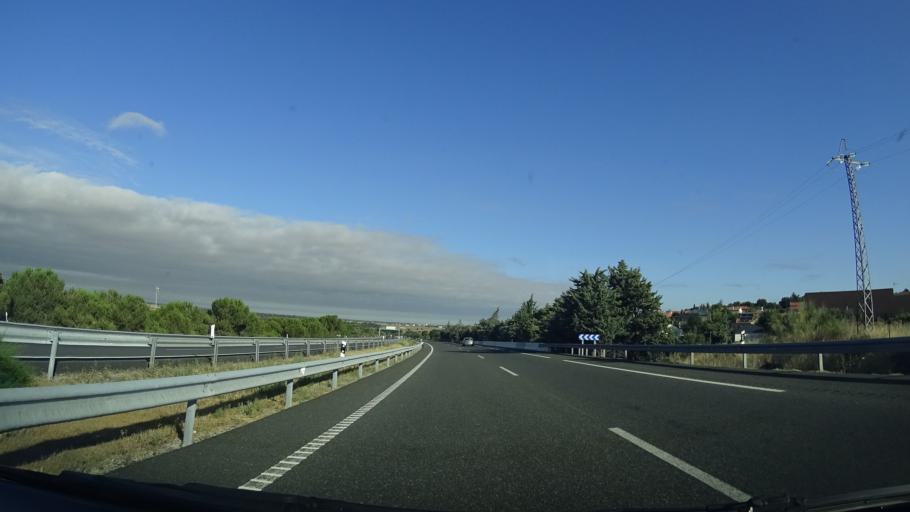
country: ES
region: Castille and Leon
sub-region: Provincia de Segovia
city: Labajos
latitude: 40.8554
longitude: -4.5478
